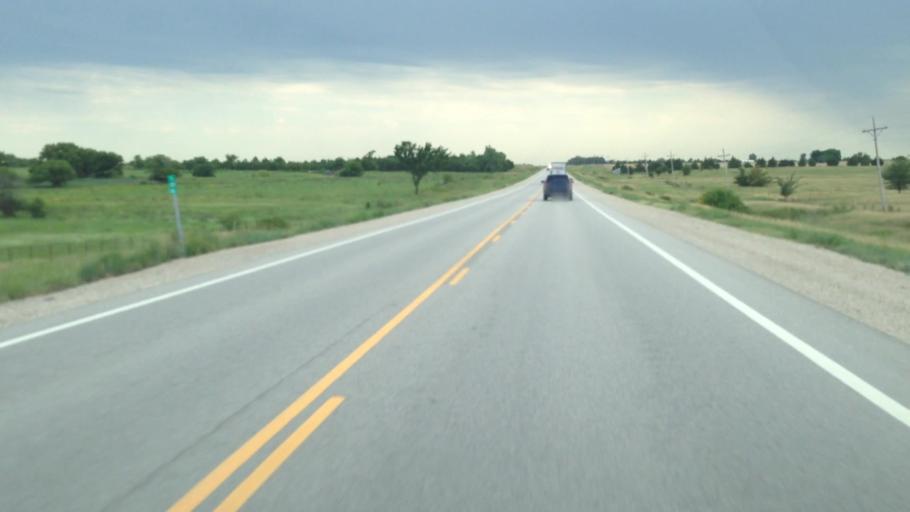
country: US
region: Kansas
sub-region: Coffey County
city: Burlington
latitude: 38.3300
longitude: -95.7290
